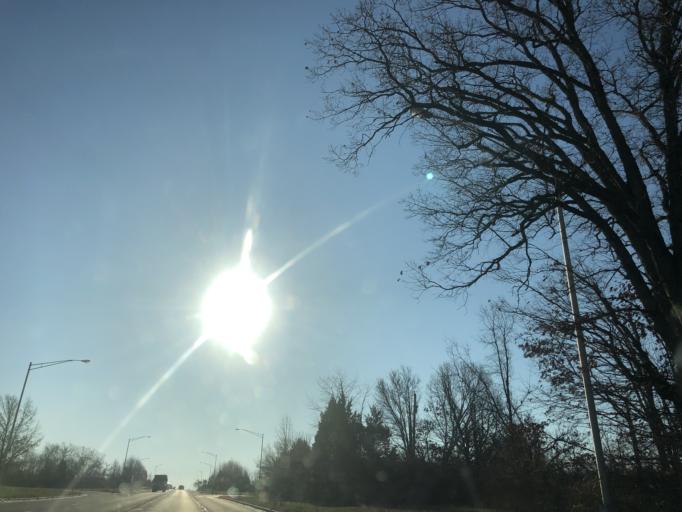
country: US
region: New Jersey
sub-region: Gloucester County
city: Wenonah
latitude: 39.7970
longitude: -75.1171
